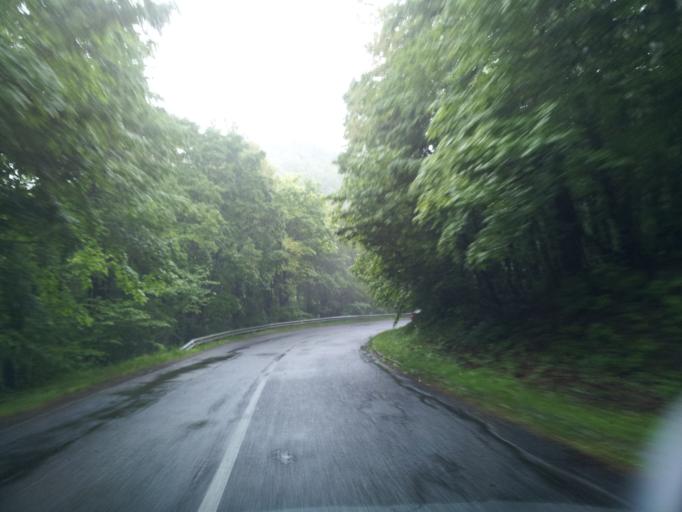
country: HU
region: Baranya
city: Hosszuheteny
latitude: 46.1730
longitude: 18.3245
